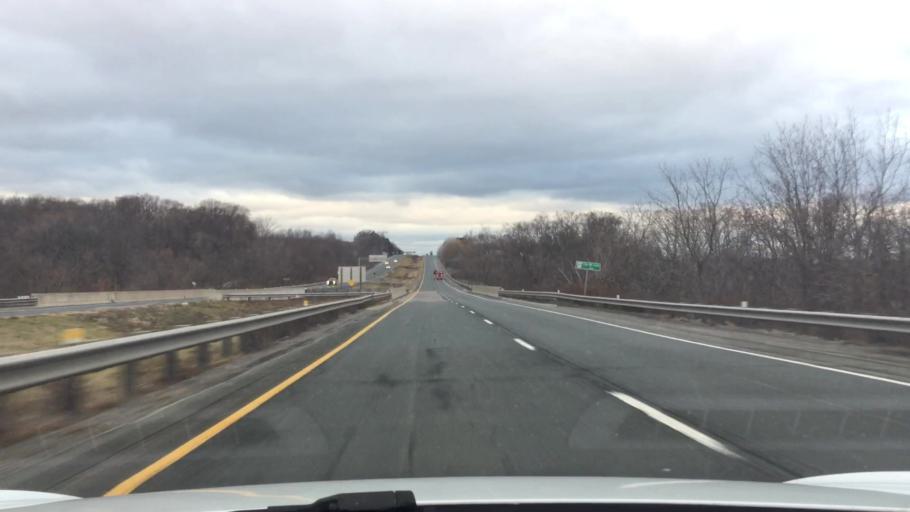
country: CA
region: Ontario
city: Niagara Falls
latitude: 43.1464
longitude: -79.0999
